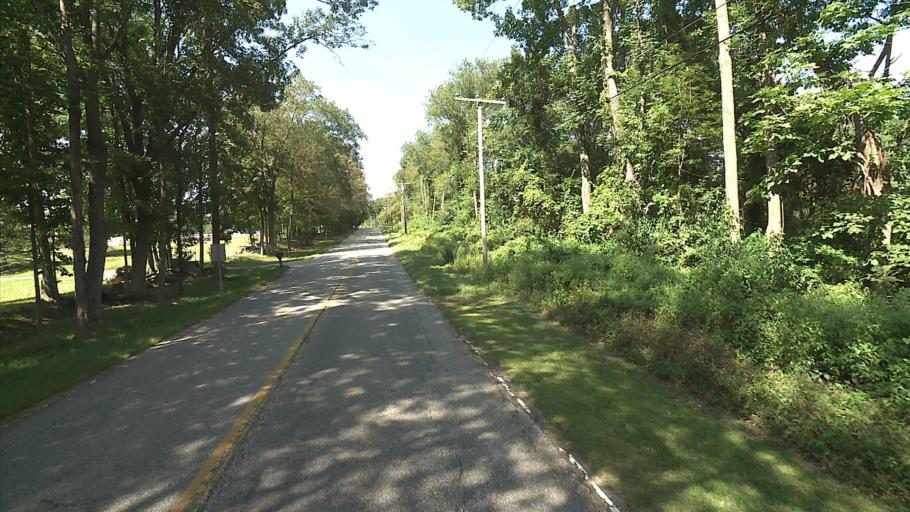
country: US
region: Connecticut
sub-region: Windham County
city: Willimantic
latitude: 41.6591
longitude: -72.2488
